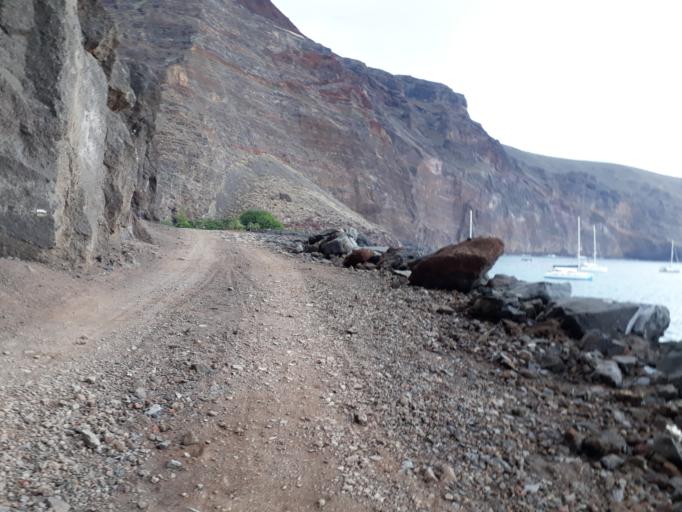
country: ES
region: Canary Islands
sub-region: Provincia de Santa Cruz de Tenerife
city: Alajero
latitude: 28.0802
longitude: -17.3265
